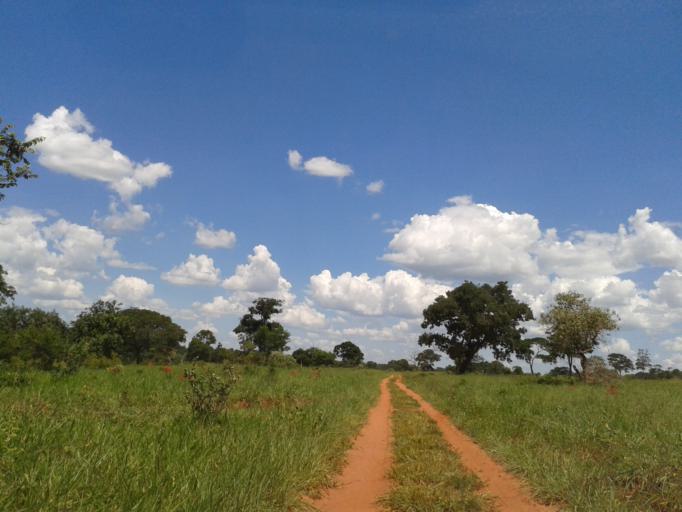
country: BR
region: Minas Gerais
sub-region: Santa Vitoria
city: Santa Vitoria
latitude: -19.1433
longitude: -50.5450
